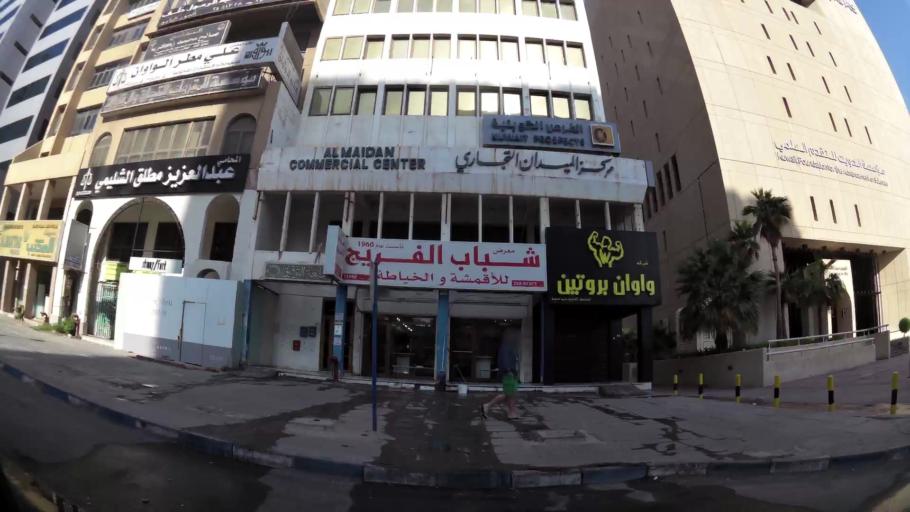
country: KW
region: Al Asimah
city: Kuwait City
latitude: 29.3774
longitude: 47.9789
